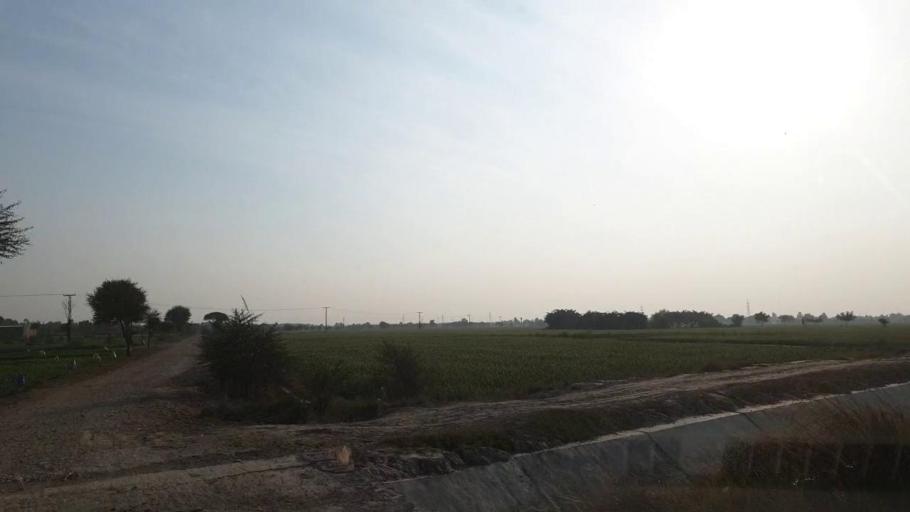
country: PK
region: Sindh
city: Matiari
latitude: 25.5911
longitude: 68.4702
